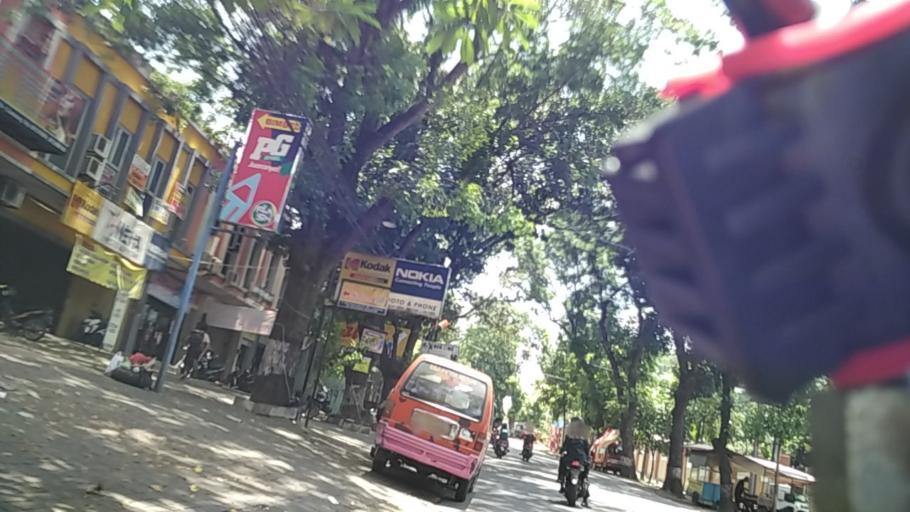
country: ID
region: Central Java
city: Semarang
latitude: -7.0088
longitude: 110.3778
